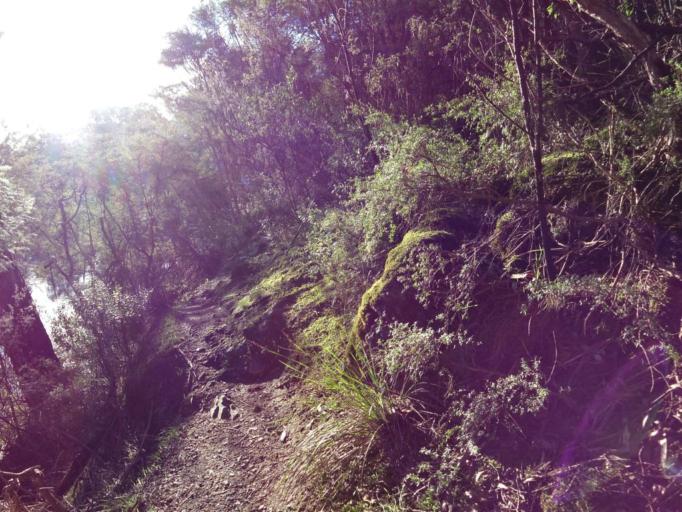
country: AU
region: Victoria
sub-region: Manningham
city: Warrandyte
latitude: -37.7332
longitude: 145.2429
